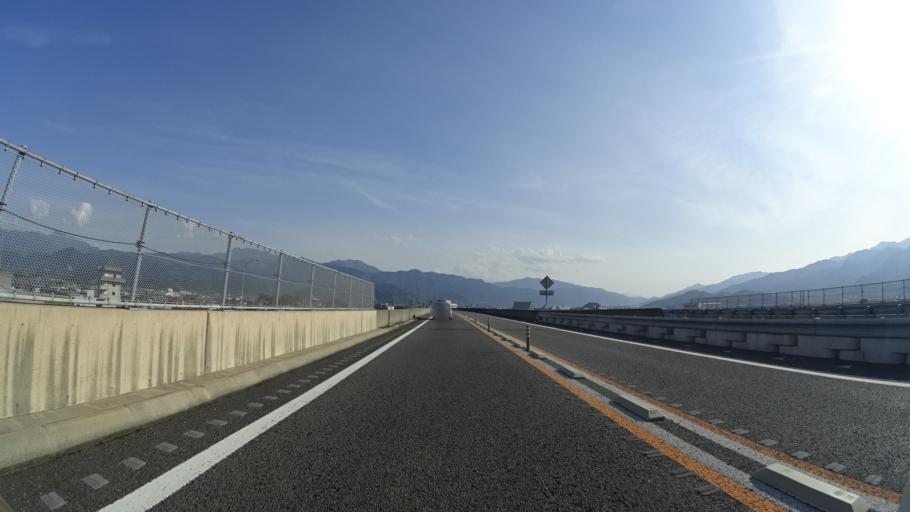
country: JP
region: Ehime
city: Saijo
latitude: 33.9183
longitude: 133.0737
